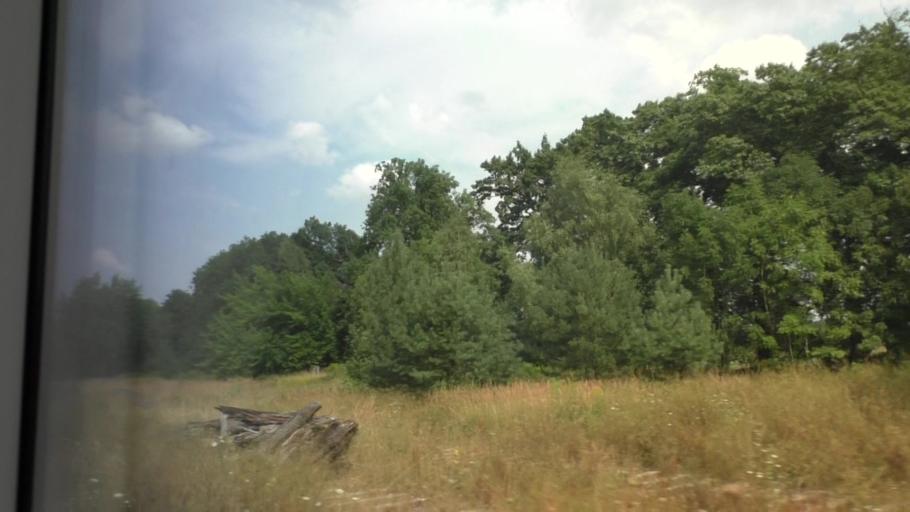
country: DE
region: Brandenburg
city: Mixdorf
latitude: 52.1667
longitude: 14.3792
